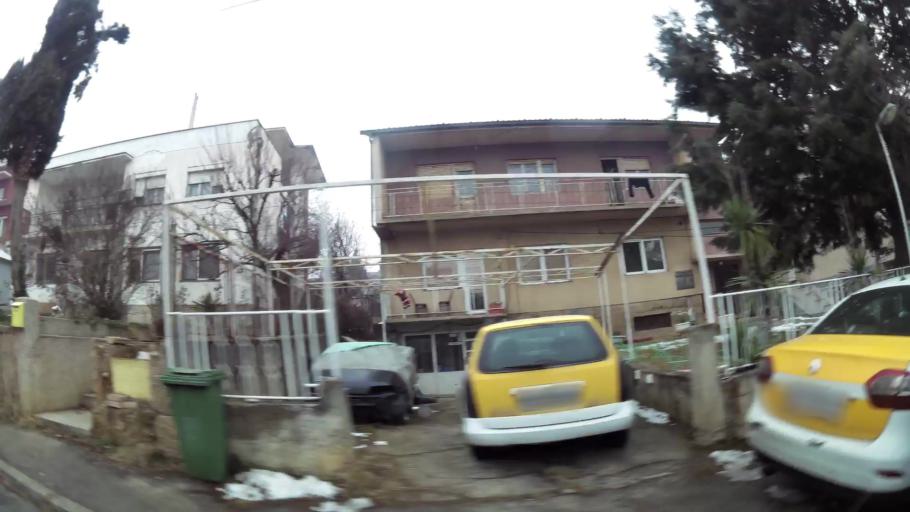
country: MK
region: Cair
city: Cair
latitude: 42.0146
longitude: 21.4542
